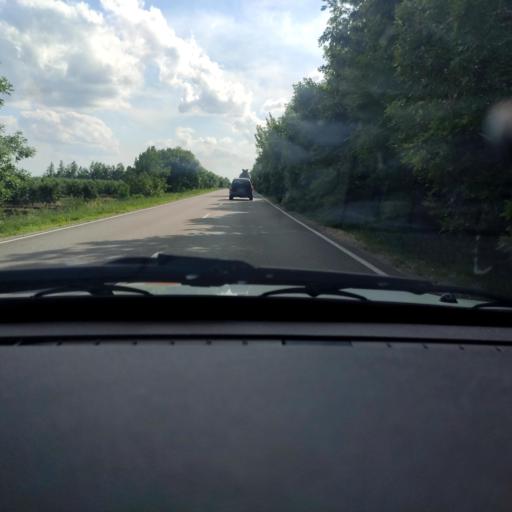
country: RU
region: Voronezj
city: Volya
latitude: 51.6977
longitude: 39.5092
